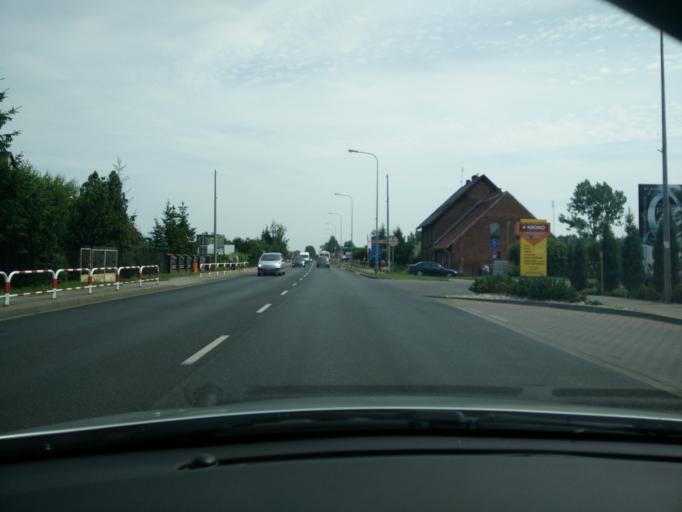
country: PL
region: Greater Poland Voivodeship
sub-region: Powiat slupecki
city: Strzalkowo
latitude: 52.3084
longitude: 17.8225
